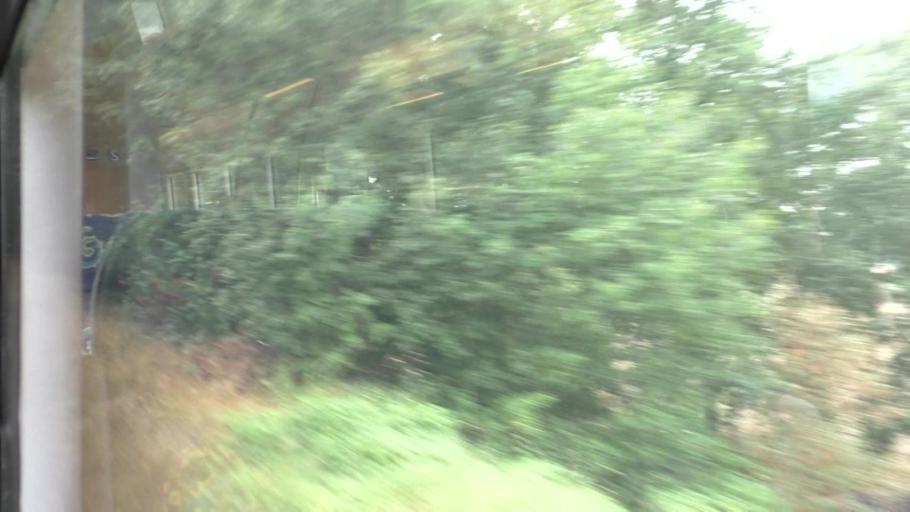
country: DE
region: Saxony
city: Goerlitz
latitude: 51.1188
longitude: 14.9672
